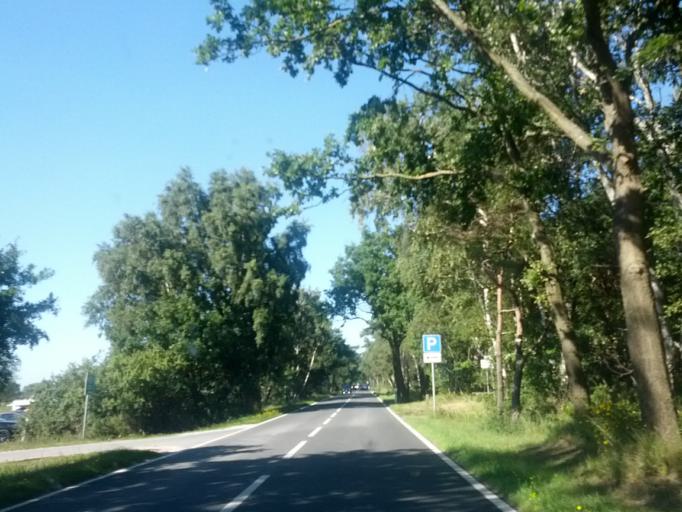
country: DE
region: Mecklenburg-Vorpommern
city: Ostseebad Gohren
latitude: 54.2968
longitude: 13.7132
